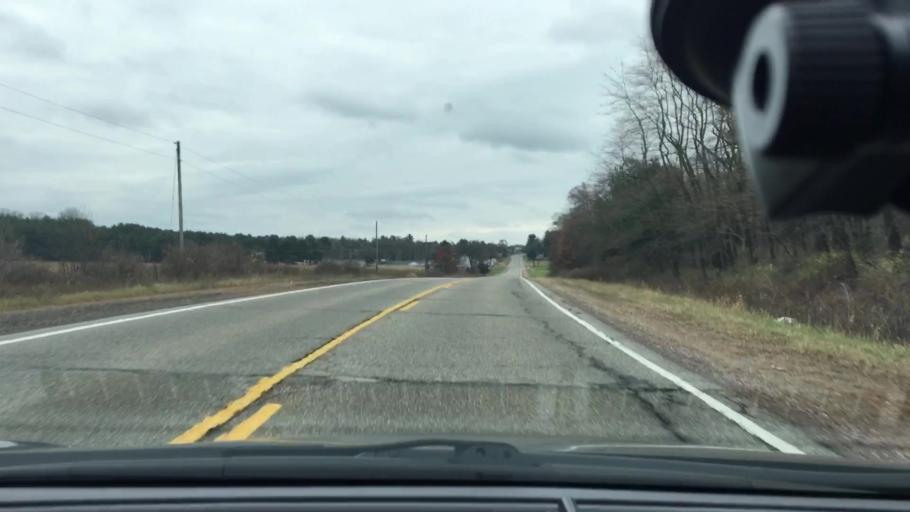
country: US
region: Wisconsin
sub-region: Columbia County
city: Wisconsin Dells
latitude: 43.6384
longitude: -89.7969
